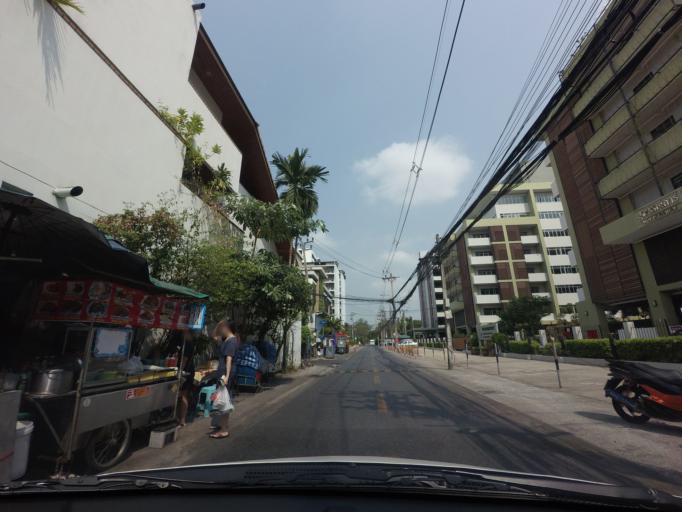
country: TH
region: Bangkok
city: Chatuchak
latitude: 13.8524
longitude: 100.5806
